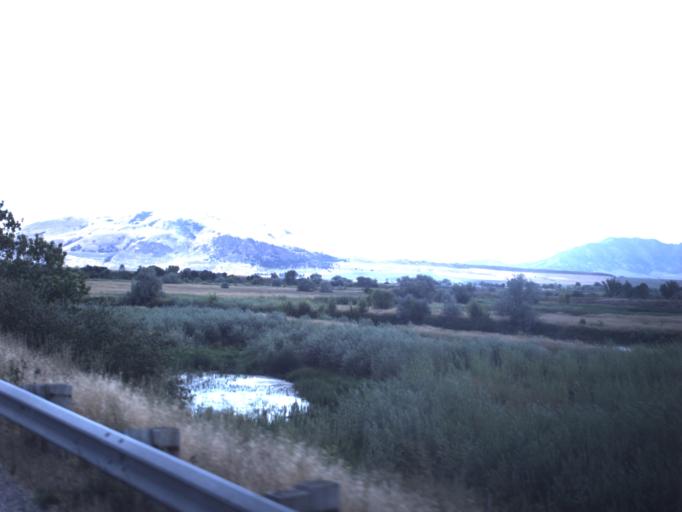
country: US
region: Utah
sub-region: Cache County
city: Lewiston
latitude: 41.9206
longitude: -111.9090
